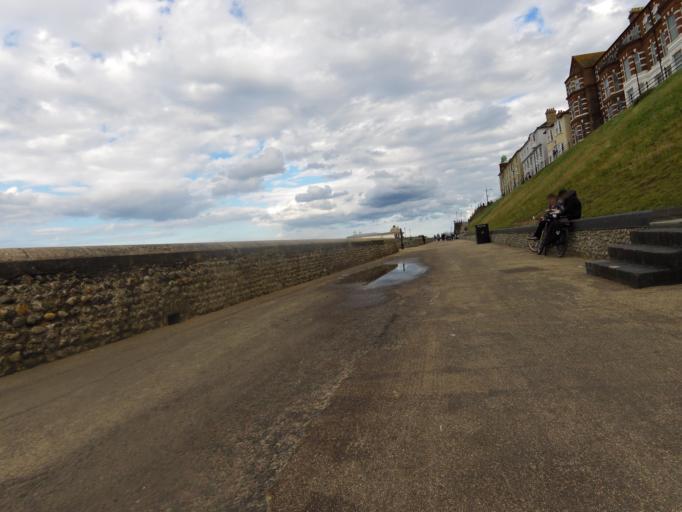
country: GB
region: England
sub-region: Norfolk
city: Cromer
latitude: 52.9330
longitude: 1.2987
